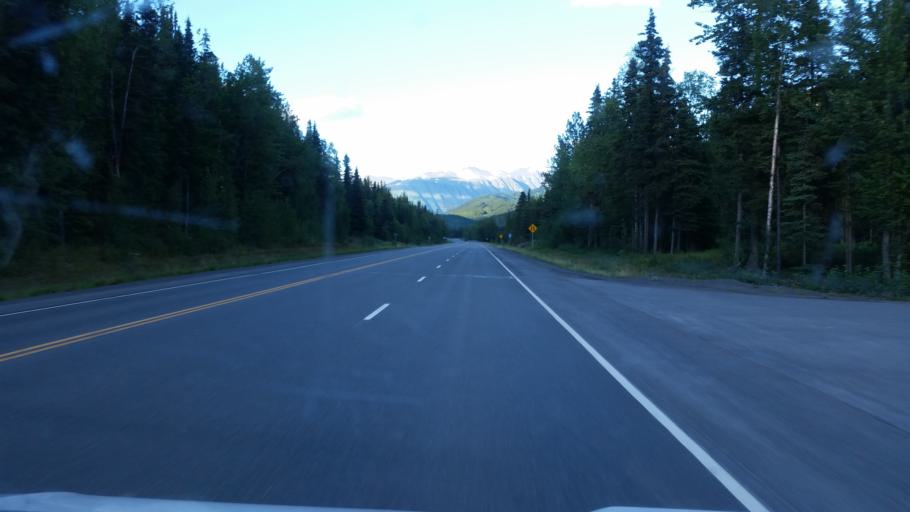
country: US
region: Alaska
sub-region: Kenai Peninsula Borough
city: Bear Creek
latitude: 60.4891
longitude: -149.7182
